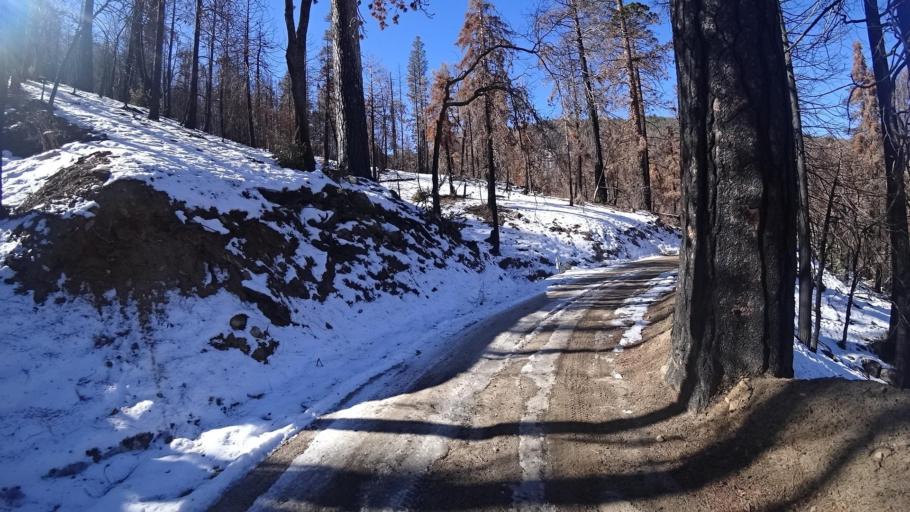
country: US
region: California
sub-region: Kern County
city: Alta Sierra
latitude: 35.7164
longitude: -118.5416
